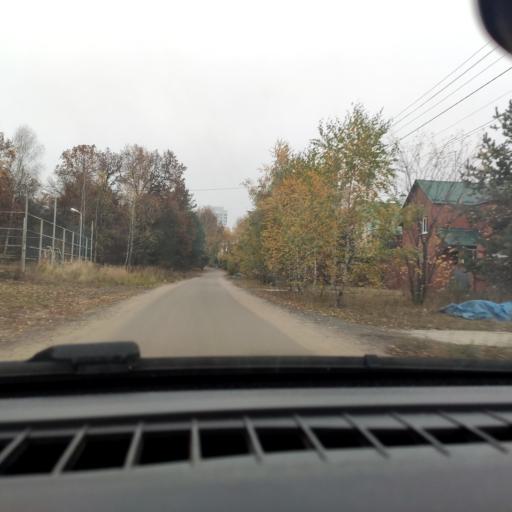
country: RU
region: Voronezj
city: Podgornoye
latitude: 51.7649
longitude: 39.1820
